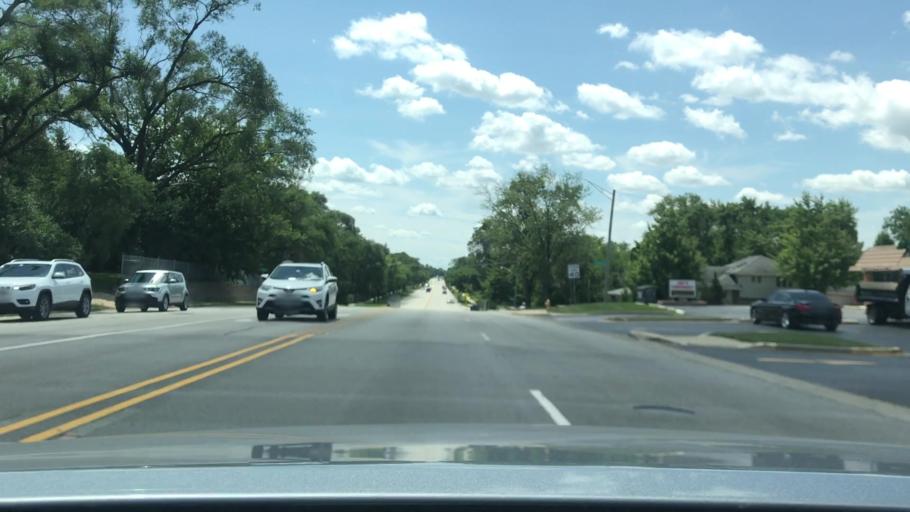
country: US
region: Illinois
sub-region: DuPage County
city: Downers Grove
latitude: 41.7726
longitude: -88.0085
